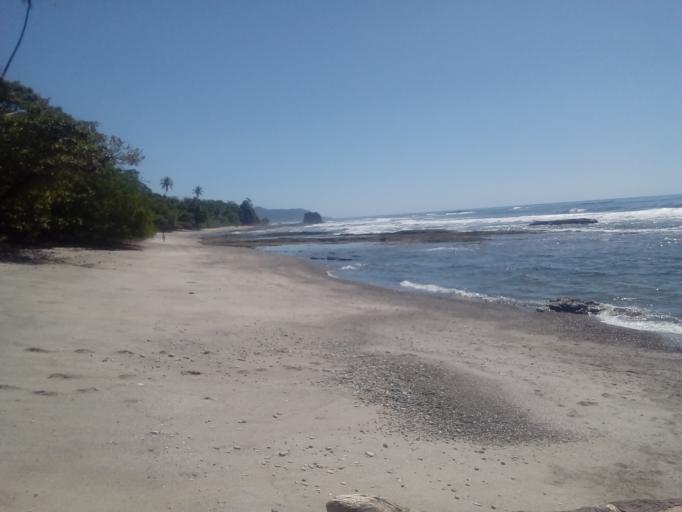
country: CR
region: Guanacaste
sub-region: Canton de Nandayure
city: Bejuco
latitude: 9.6588
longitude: -85.1850
